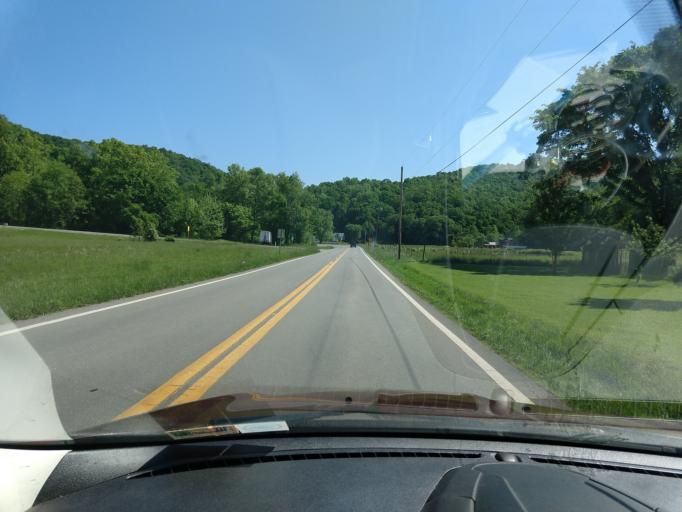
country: US
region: West Virginia
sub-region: Gilmer County
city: Glenville
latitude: 38.8945
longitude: -80.7313
